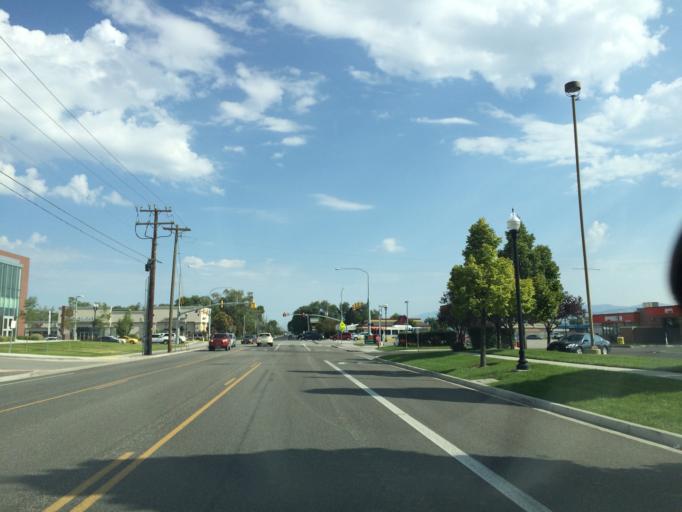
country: US
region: Utah
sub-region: Salt Lake County
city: West Valley City
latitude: 40.6955
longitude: -111.9771
